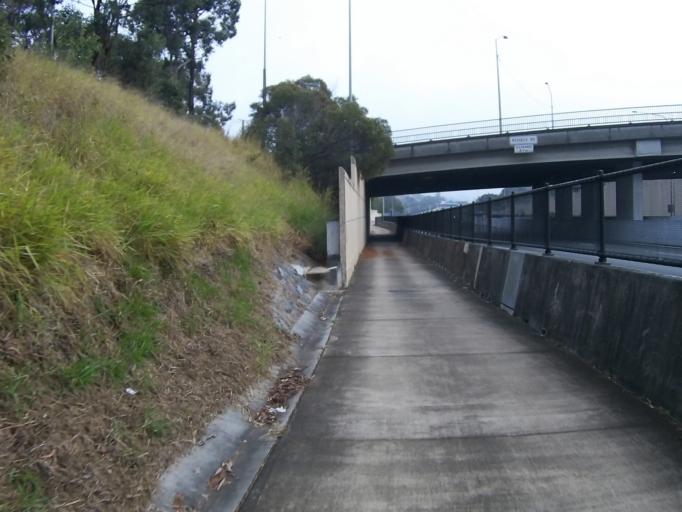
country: AU
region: Queensland
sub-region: Brisbane
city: Upper Mount Gravatt
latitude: -27.5618
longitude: 153.0770
